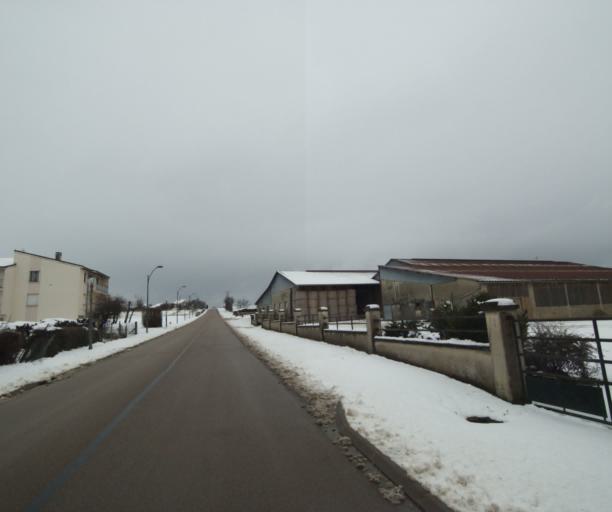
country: FR
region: Champagne-Ardenne
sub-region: Departement de la Haute-Marne
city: Laneuville-a-Remy
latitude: 48.4171
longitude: 4.8377
